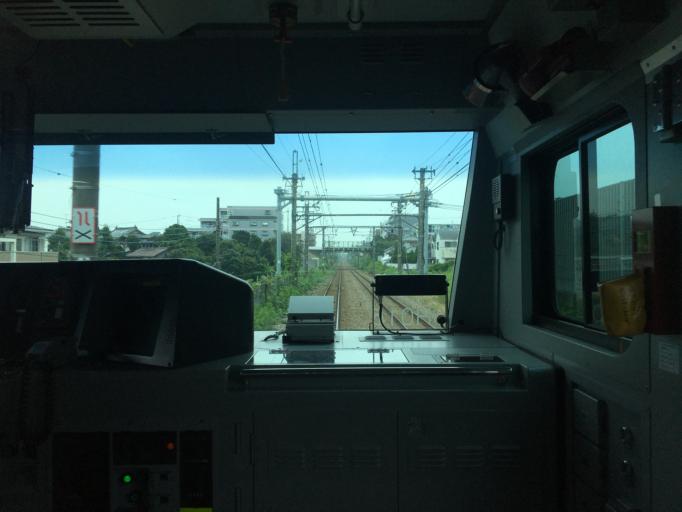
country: JP
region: Tokyo
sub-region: Machida-shi
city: Machida
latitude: 35.5303
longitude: 139.5041
